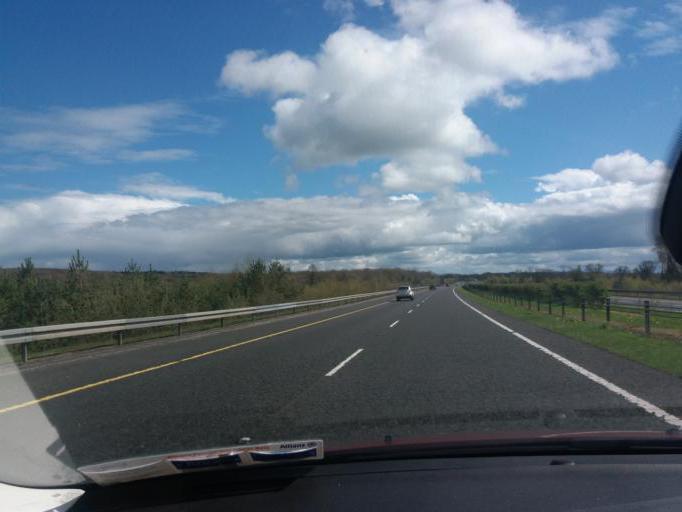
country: IE
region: Leinster
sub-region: Kildare
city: Monasterevin
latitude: 53.1144
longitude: -7.0814
